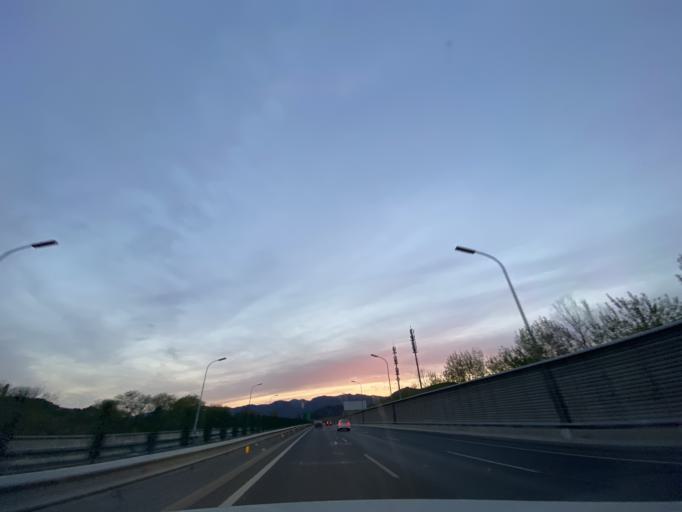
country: CN
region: Beijing
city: Haidian
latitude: 40.0017
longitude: 116.2540
